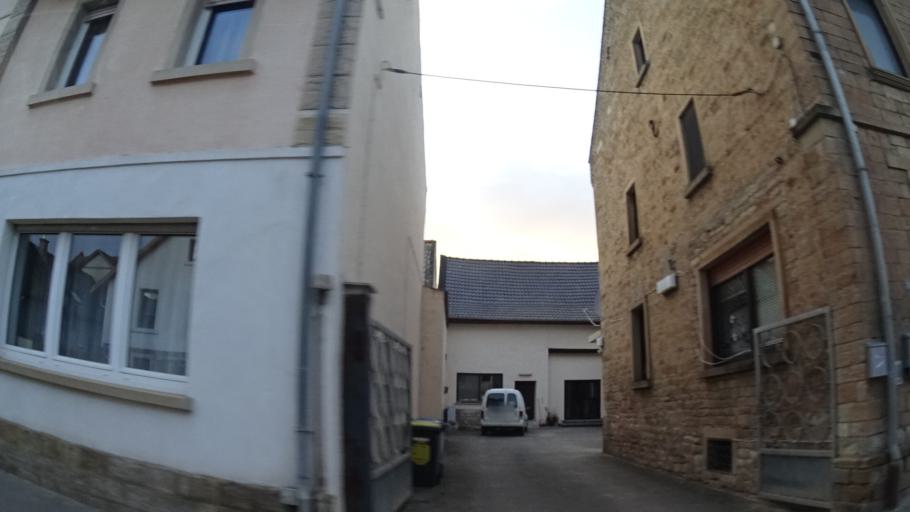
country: DE
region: Rheinland-Pfalz
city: Armsheim
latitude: 49.8094
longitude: 8.0570
